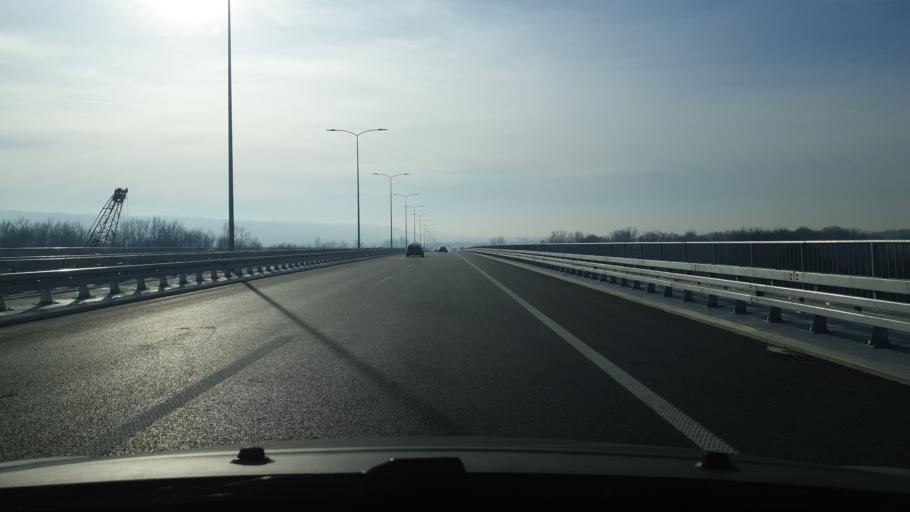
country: RS
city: Baric
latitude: 44.6642
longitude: 20.2442
